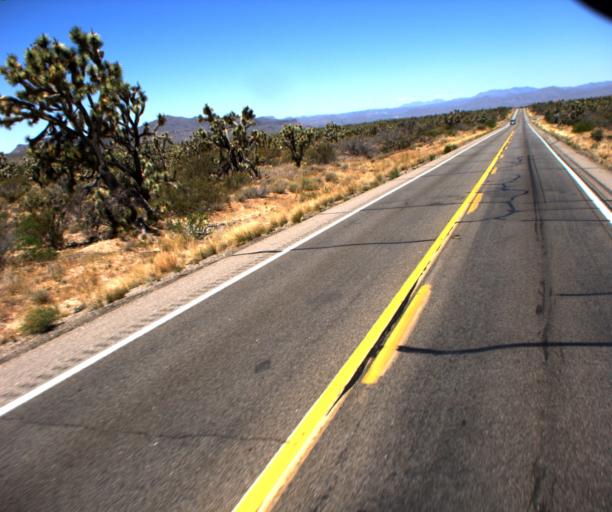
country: US
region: Arizona
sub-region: Yavapai County
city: Congress
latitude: 34.2574
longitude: -113.0861
